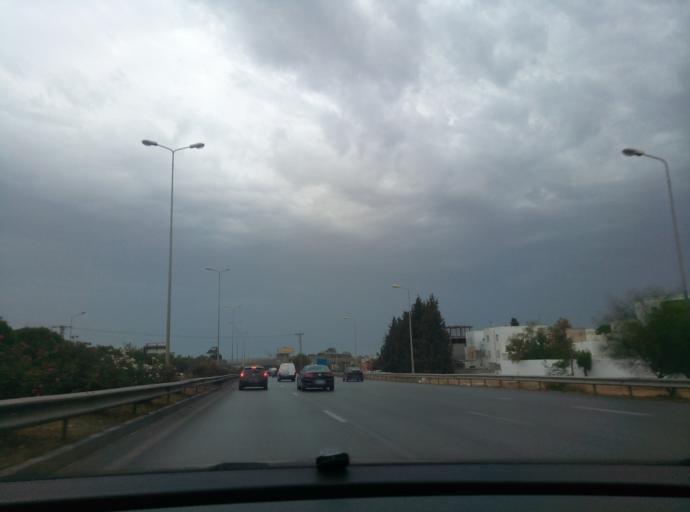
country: TN
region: Bin 'Arus
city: Ben Arous
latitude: 36.7441
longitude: 10.2120
